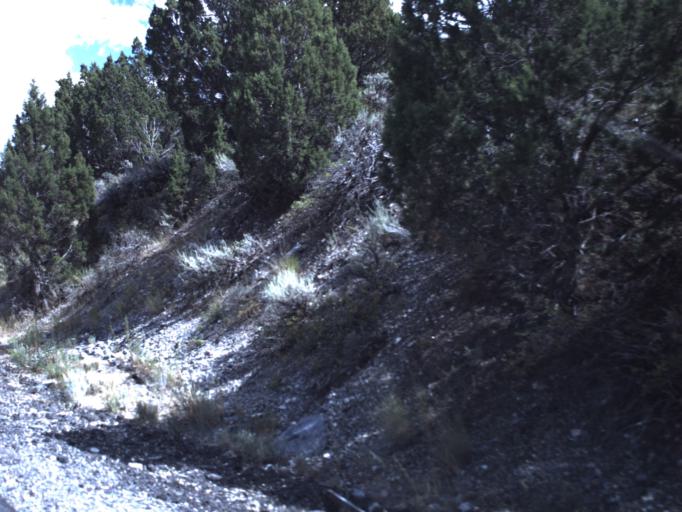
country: US
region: Utah
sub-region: Tooele County
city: Grantsville
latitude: 40.3462
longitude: -112.5891
